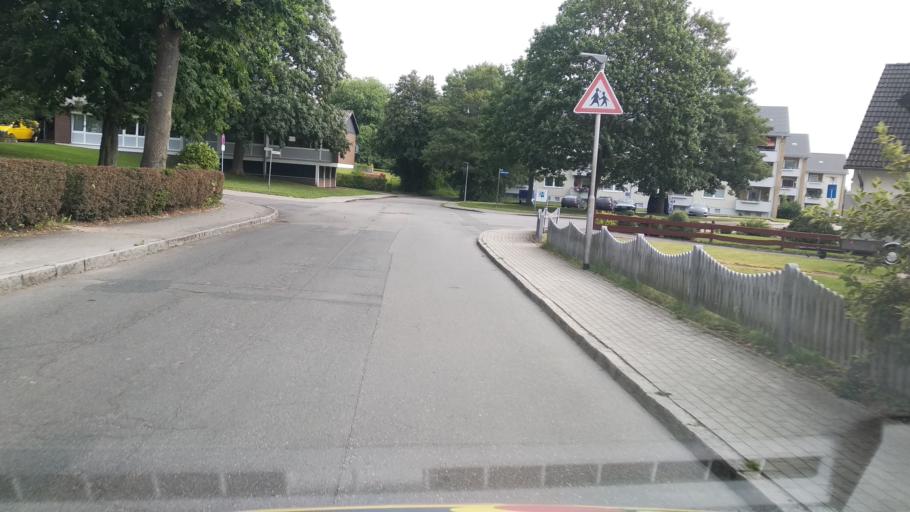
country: DE
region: Schleswig-Holstein
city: Schleswig
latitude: 54.5212
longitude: 9.5763
